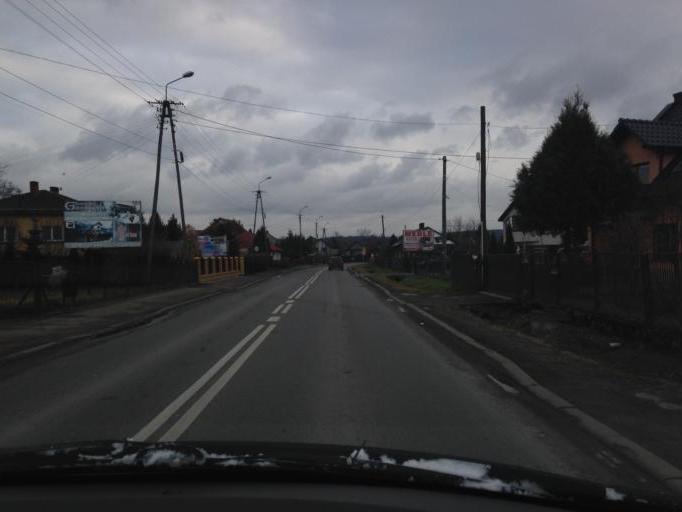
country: PL
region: Lesser Poland Voivodeship
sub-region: Powiat wielicki
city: Gdow
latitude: 49.9047
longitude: 20.2056
